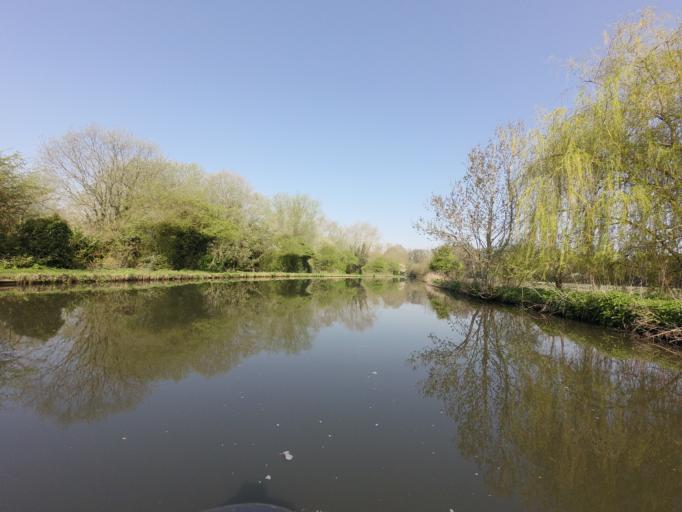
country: GB
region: England
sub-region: Hertfordshire
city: Bovingdon
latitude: 51.7483
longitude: -0.5271
